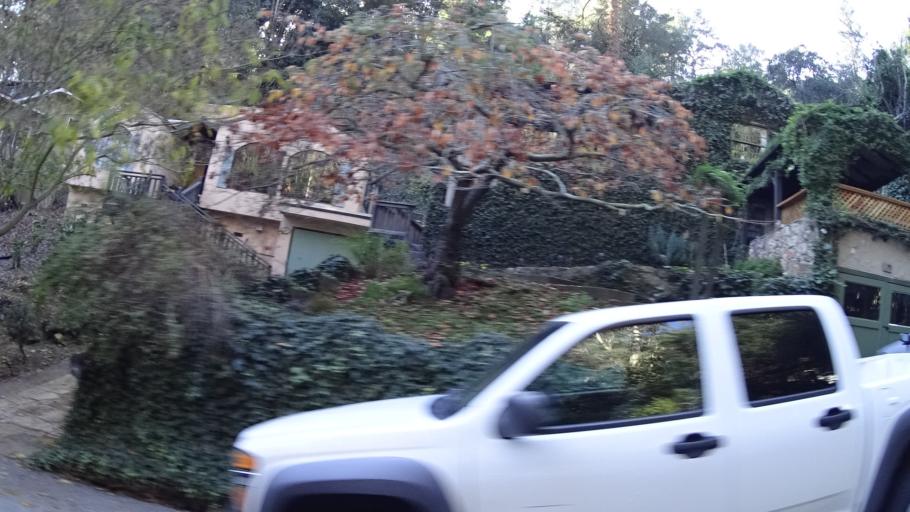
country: US
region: California
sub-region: Alameda County
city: Piedmont
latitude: 37.8425
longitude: -122.2102
